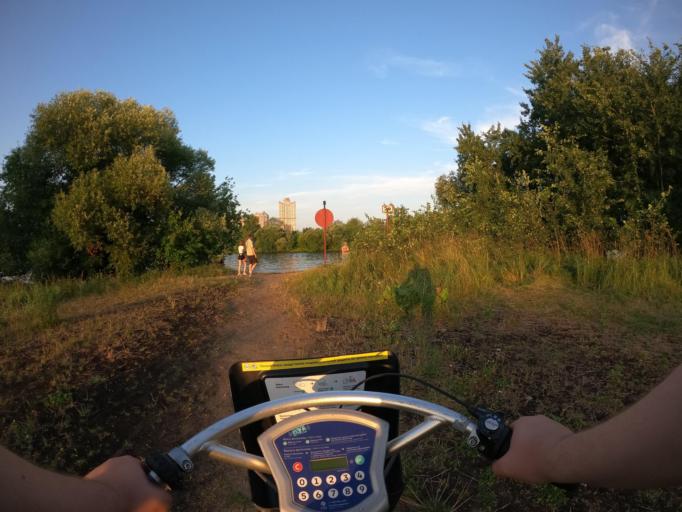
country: RU
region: Moscow
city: Shchukino
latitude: 55.8075
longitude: 37.4311
